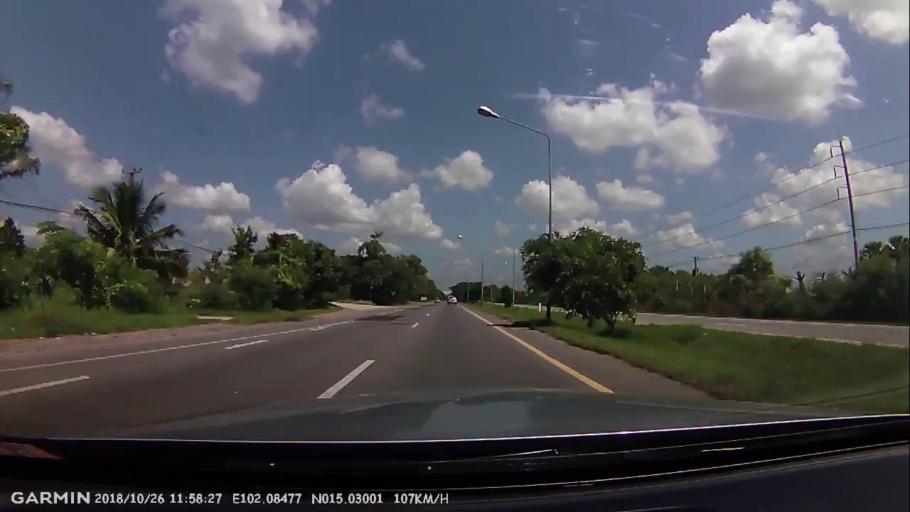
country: TH
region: Nakhon Ratchasima
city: Nakhon Ratchasima
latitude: 15.0304
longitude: 102.0849
